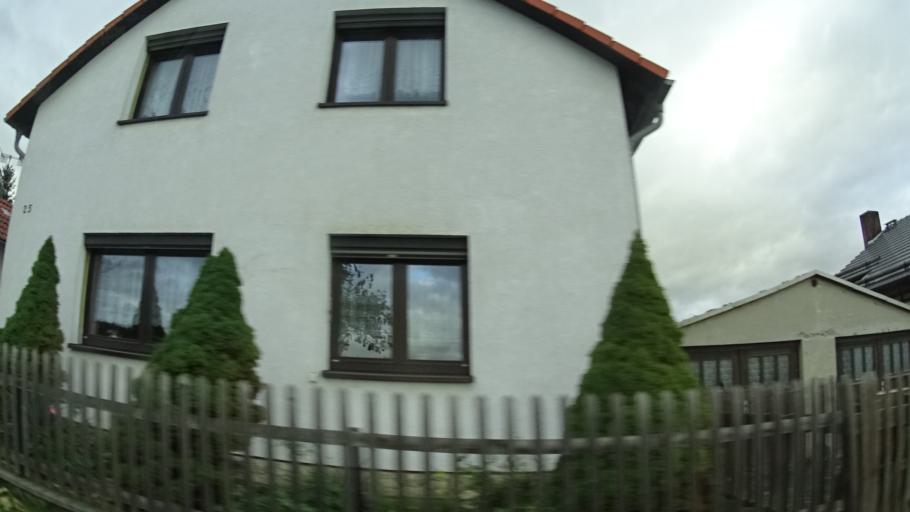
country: DE
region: Thuringia
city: Bodelwitz
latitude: 50.6890
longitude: 11.6212
